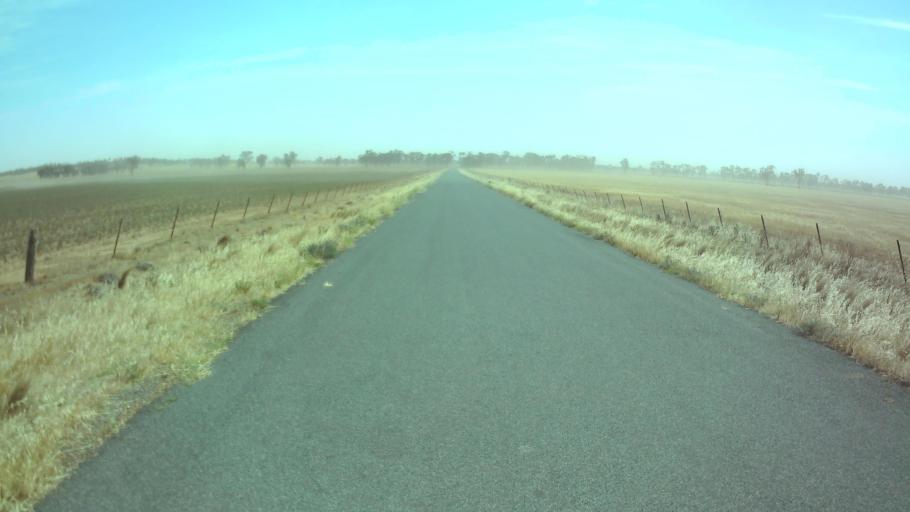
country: AU
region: New South Wales
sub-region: Weddin
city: Grenfell
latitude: -33.7260
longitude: 147.9989
